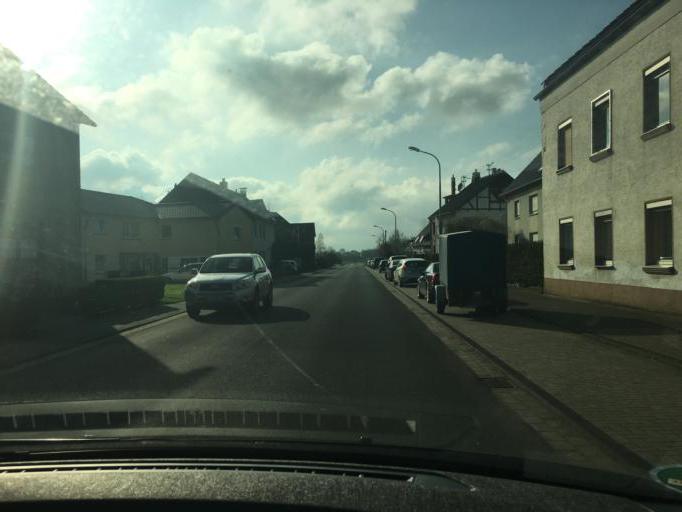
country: DE
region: North Rhine-Westphalia
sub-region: Regierungsbezirk Koln
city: Weilerswist
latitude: 50.7365
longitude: 6.8862
